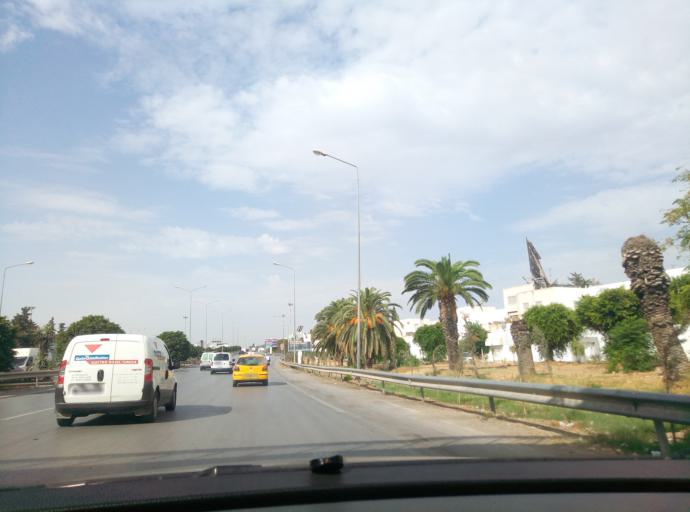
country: TN
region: Tunis
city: Tunis
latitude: 36.8421
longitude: 10.1721
